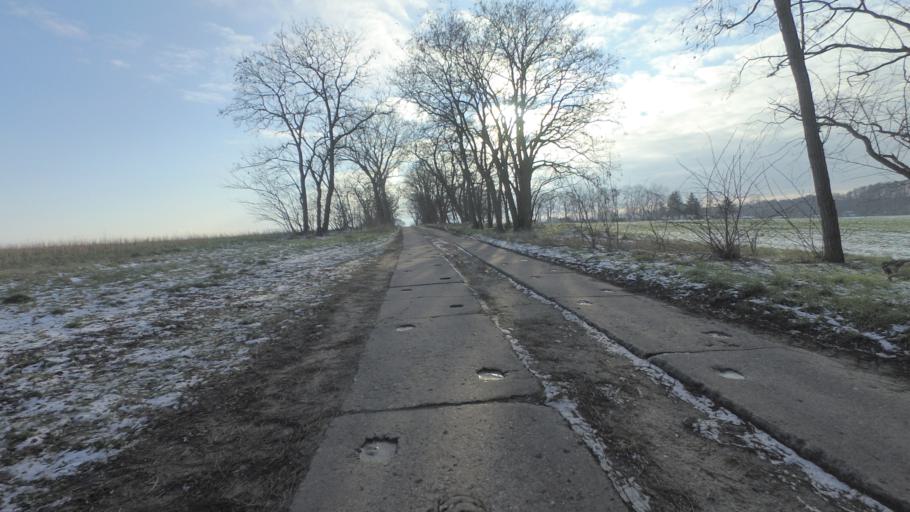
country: DE
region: Brandenburg
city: Zossen
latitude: 52.2307
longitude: 13.4171
